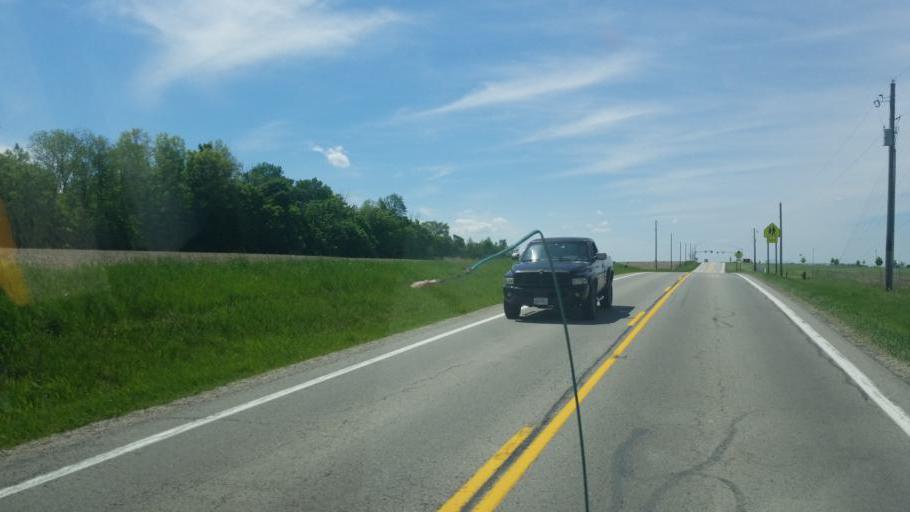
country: US
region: Ohio
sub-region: Huron County
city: Willard
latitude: 41.0750
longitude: -82.9137
